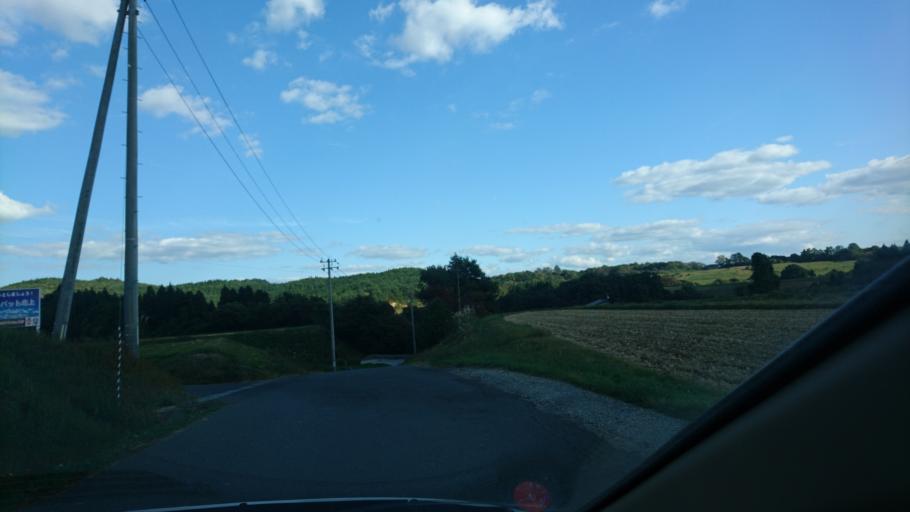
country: JP
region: Iwate
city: Kitakami
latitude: 39.2485
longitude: 141.1282
